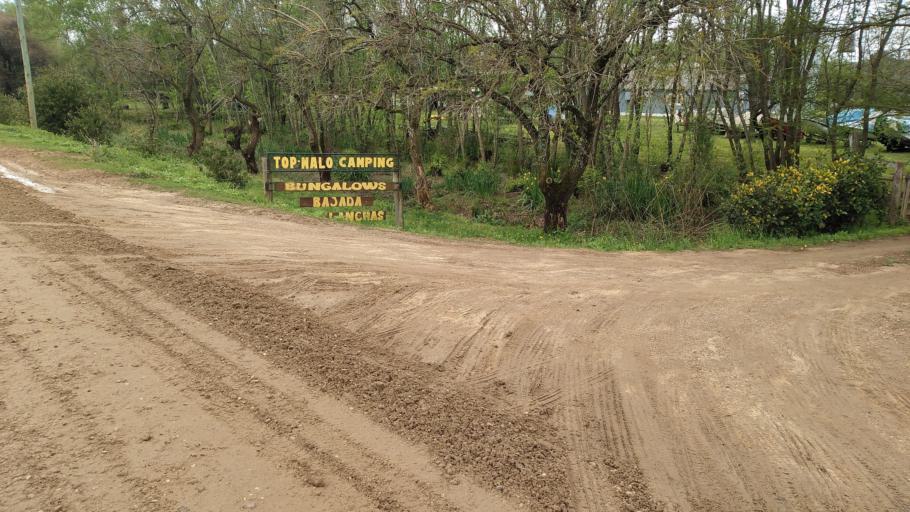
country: AR
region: Entre Rios
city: Villa Paranacito
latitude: -33.7184
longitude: -58.6810
